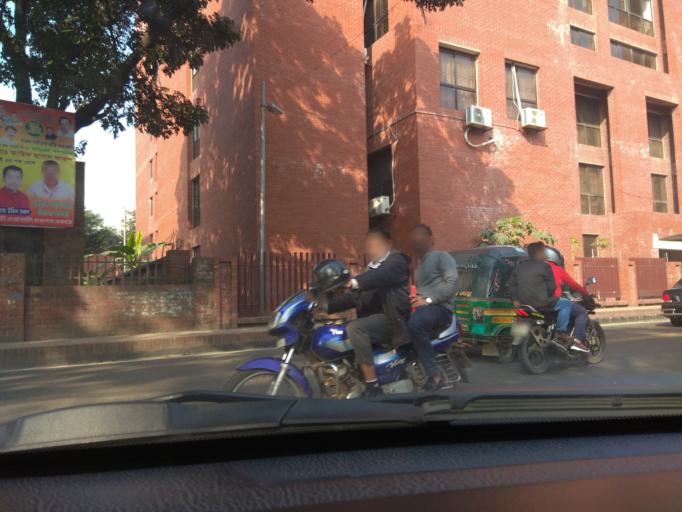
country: BD
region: Dhaka
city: Azimpur
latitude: 23.7683
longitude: 90.3724
